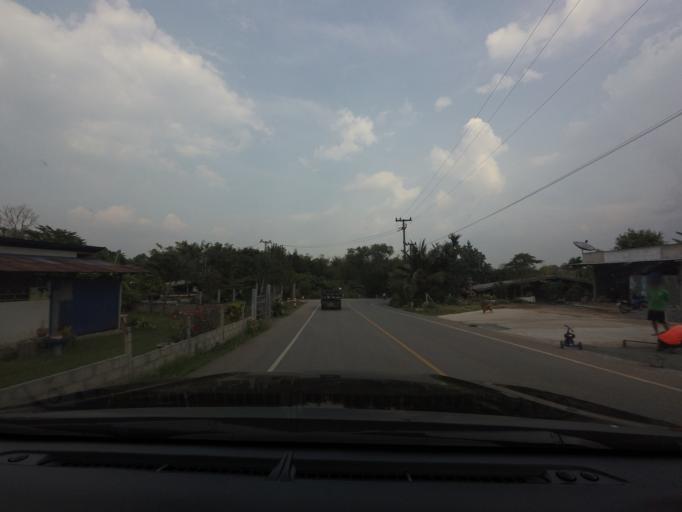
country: TH
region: Nakhon Ratchasima
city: Wang Nam Khiao
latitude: 14.4156
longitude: 101.7950
